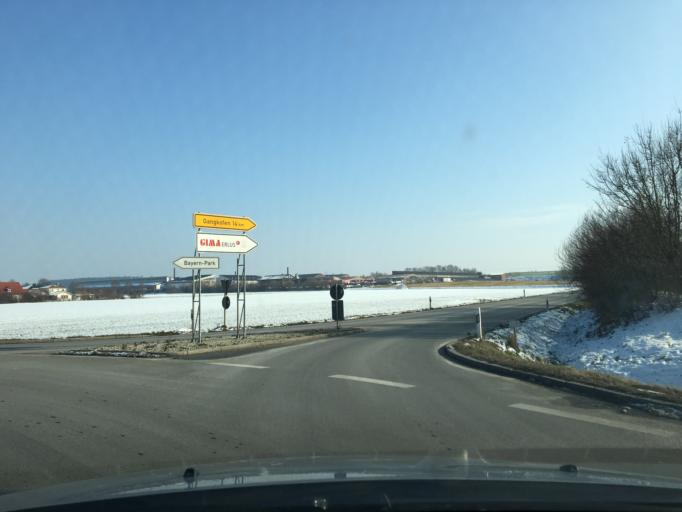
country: DE
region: Bavaria
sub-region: Lower Bavaria
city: Frontenhausen
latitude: 48.5504
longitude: 12.5452
